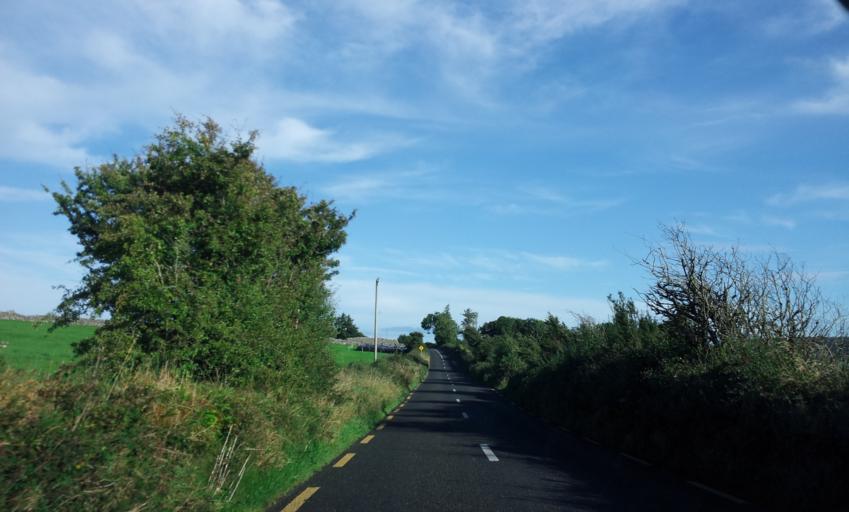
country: IE
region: Munster
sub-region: An Clar
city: Ennis
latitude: 52.9823
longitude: -9.1247
